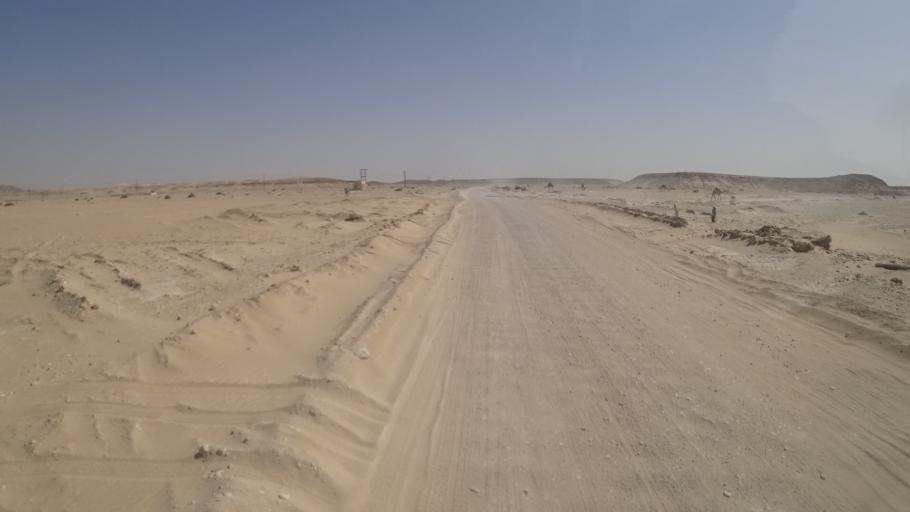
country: YE
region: Al Mahrah
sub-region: Shahan
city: Shihan as Sufla
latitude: 17.8739
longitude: 52.6077
